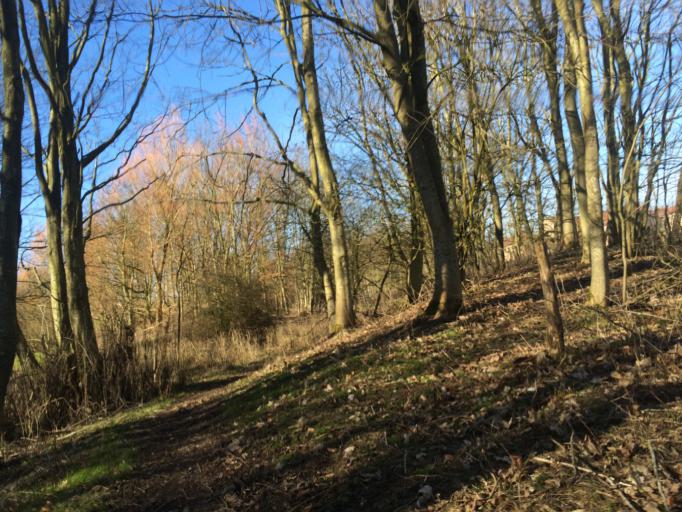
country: GB
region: Scotland
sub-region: Fife
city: Thornton
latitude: 56.1726
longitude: -3.1586
